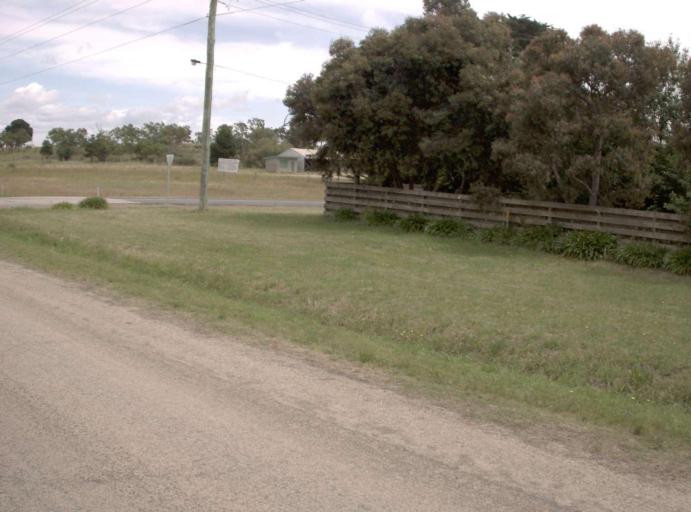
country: AU
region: Victoria
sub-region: Wellington
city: Sale
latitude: -37.9728
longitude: 146.9947
